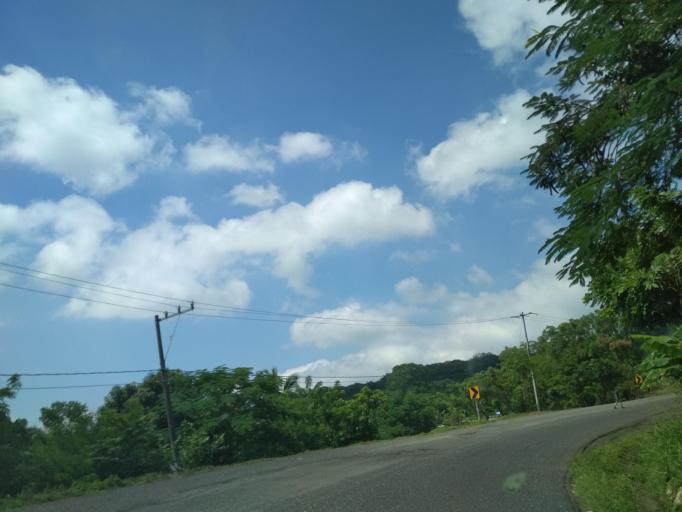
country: MX
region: Veracruz
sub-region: San Andres Tuxtla
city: Texcaltitan Xoteapan (Texcaltitan)
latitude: 18.4367
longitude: -95.2633
